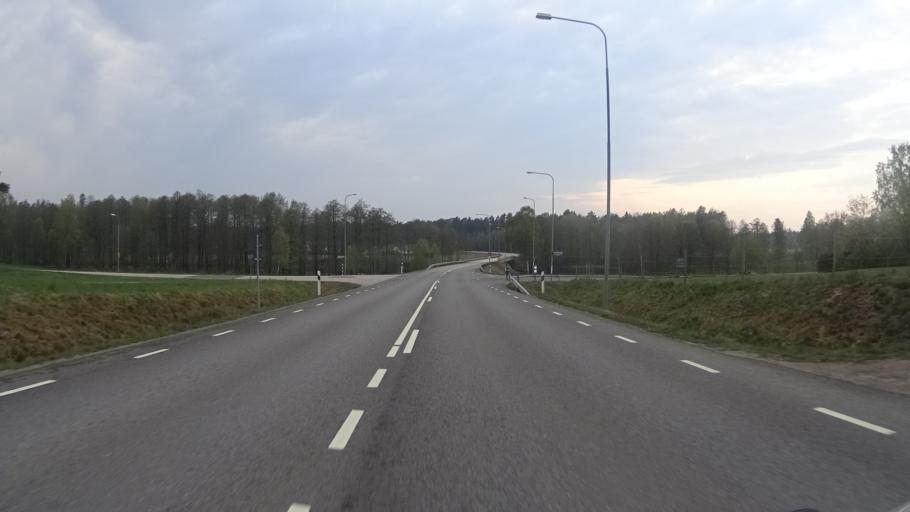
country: SE
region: Kronoberg
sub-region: Ljungby Kommun
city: Ljungby
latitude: 56.8423
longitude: 13.9720
